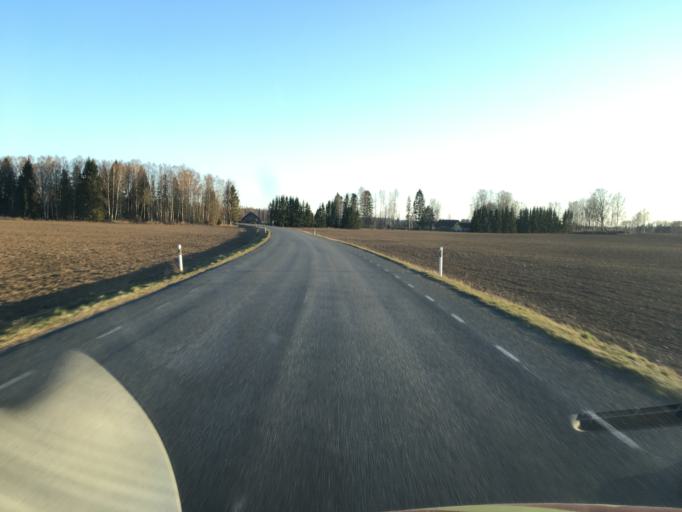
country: EE
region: Raplamaa
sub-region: Kehtna vald
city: Kehtna
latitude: 59.0152
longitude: 24.9212
